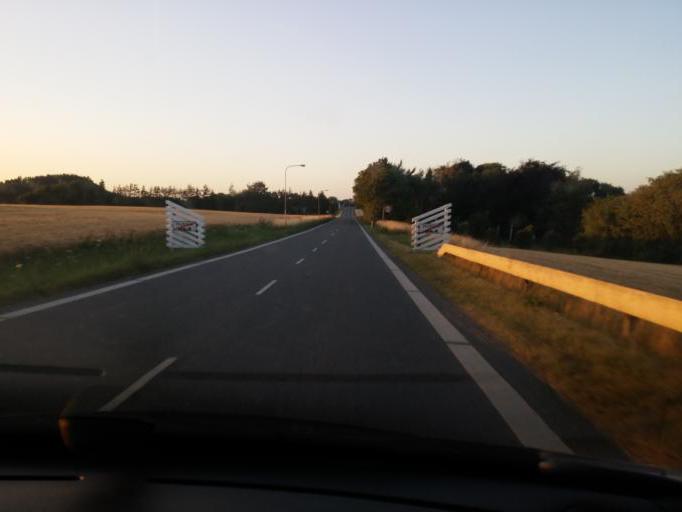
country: DK
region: South Denmark
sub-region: Langeland Kommune
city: Rudkobing
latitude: 54.8349
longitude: 10.7033
